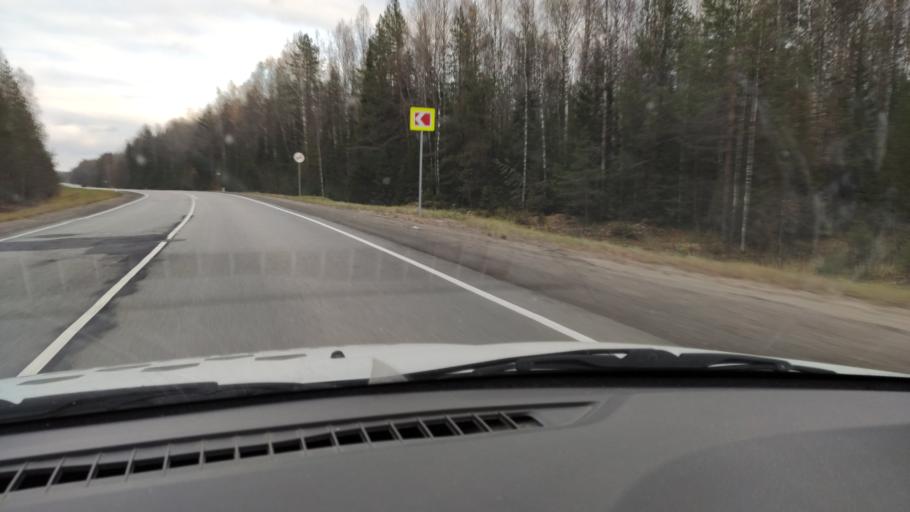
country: RU
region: Kirov
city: Chernaya Kholunitsa
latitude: 58.8304
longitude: 51.7620
